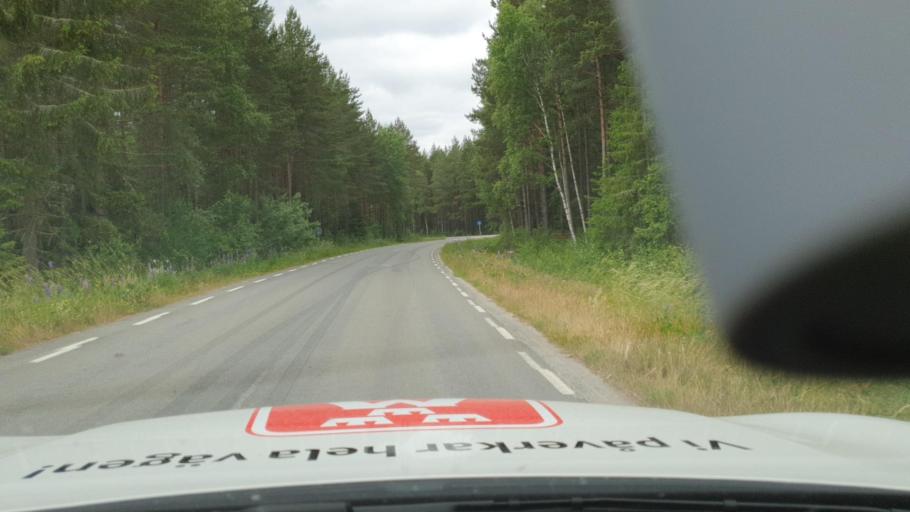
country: SE
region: Vaestra Goetaland
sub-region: Tidaholms Kommun
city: Olofstorp
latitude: 58.1942
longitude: 14.0271
